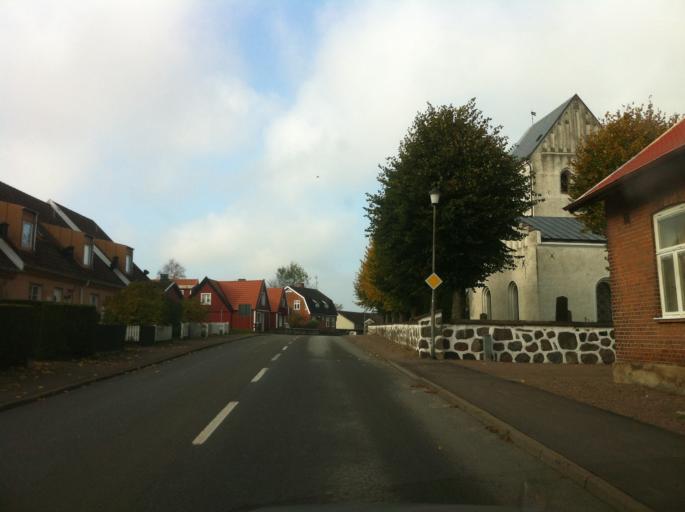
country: SE
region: Skane
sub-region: Helsingborg
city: Glumslov
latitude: 55.9324
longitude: 12.8744
